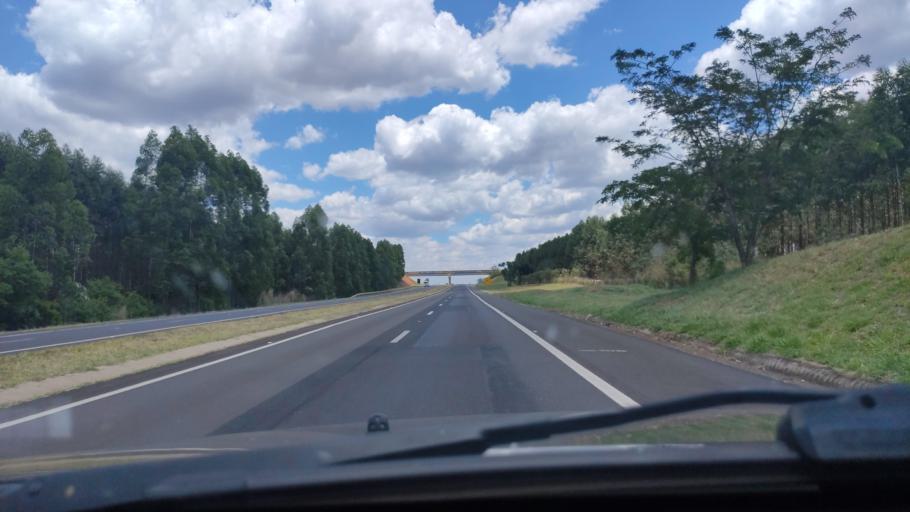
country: BR
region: Sao Paulo
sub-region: Duartina
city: Duartina
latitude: -22.5405
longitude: -49.3478
